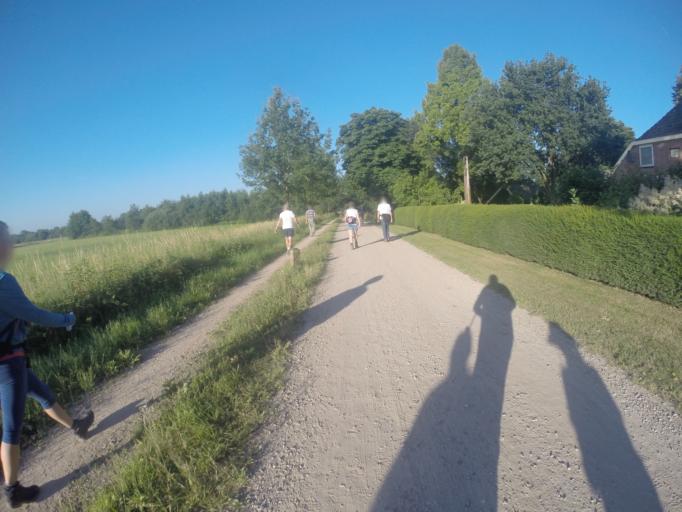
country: NL
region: Gelderland
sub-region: Gemeente Lochem
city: Barchem
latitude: 52.1175
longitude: 6.4305
